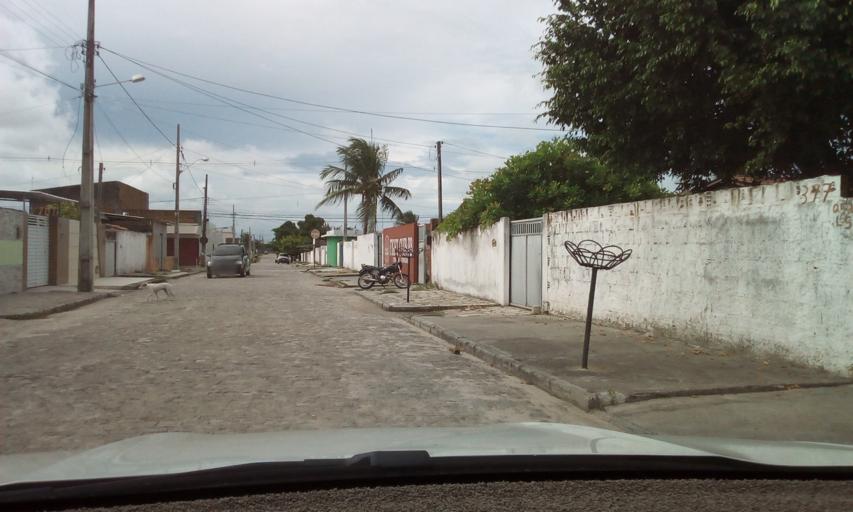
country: BR
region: Paraiba
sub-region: Joao Pessoa
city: Joao Pessoa
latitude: -7.1775
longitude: -34.8337
